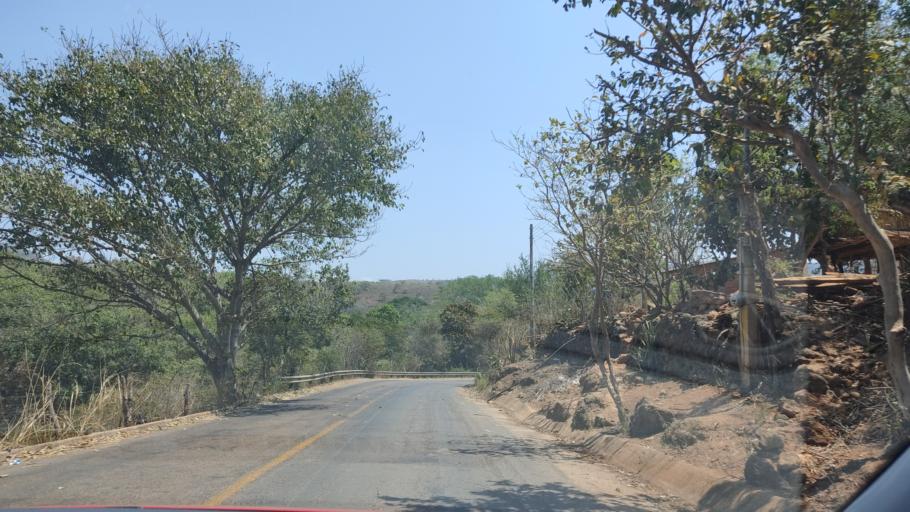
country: MX
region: Nayarit
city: Puga
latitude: 21.5783
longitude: -104.7801
